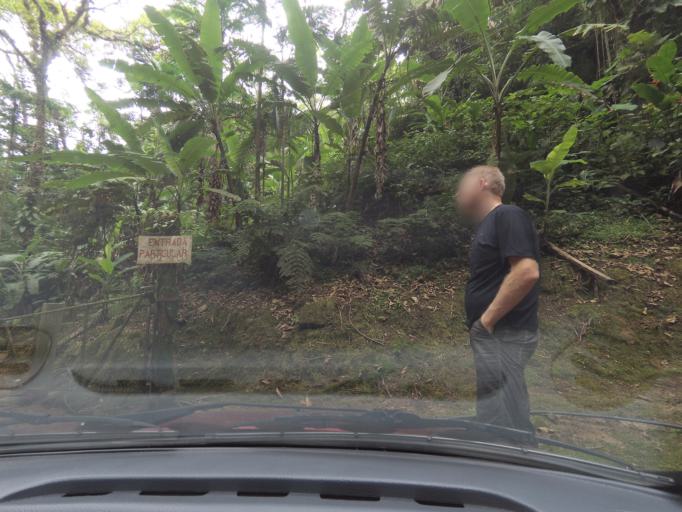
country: BR
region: Santa Catarina
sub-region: Brusque
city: Brusque
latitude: -27.0417
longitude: -48.9975
